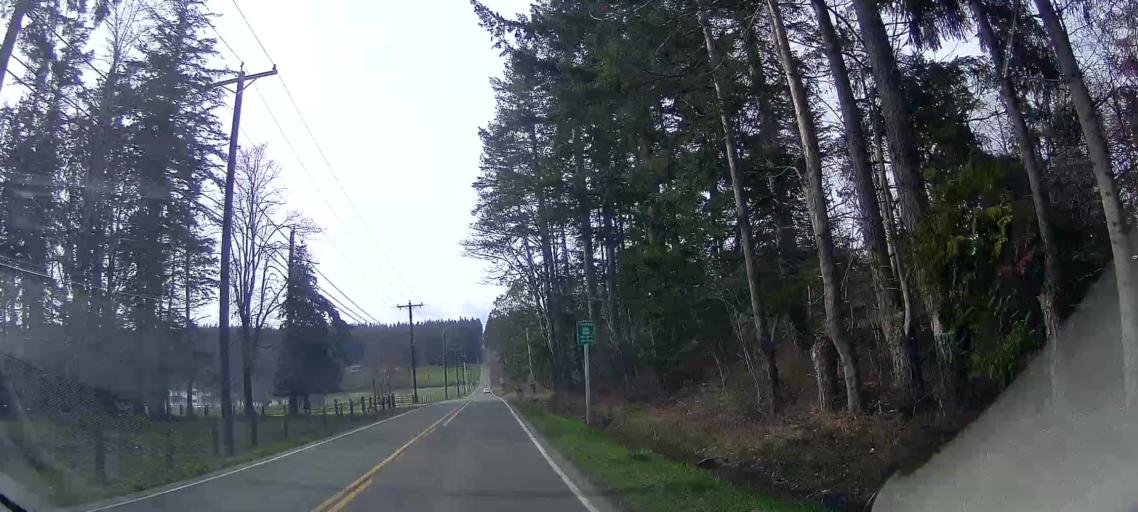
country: US
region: Washington
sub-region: Island County
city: Camano
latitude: 48.1383
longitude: -122.4721
